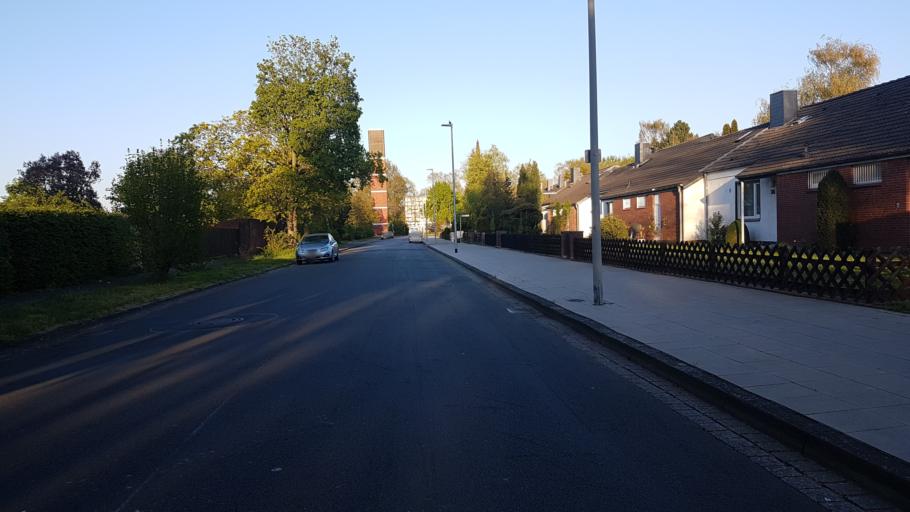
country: DE
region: Lower Saxony
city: Langenhagen
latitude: 52.4132
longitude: 9.7452
